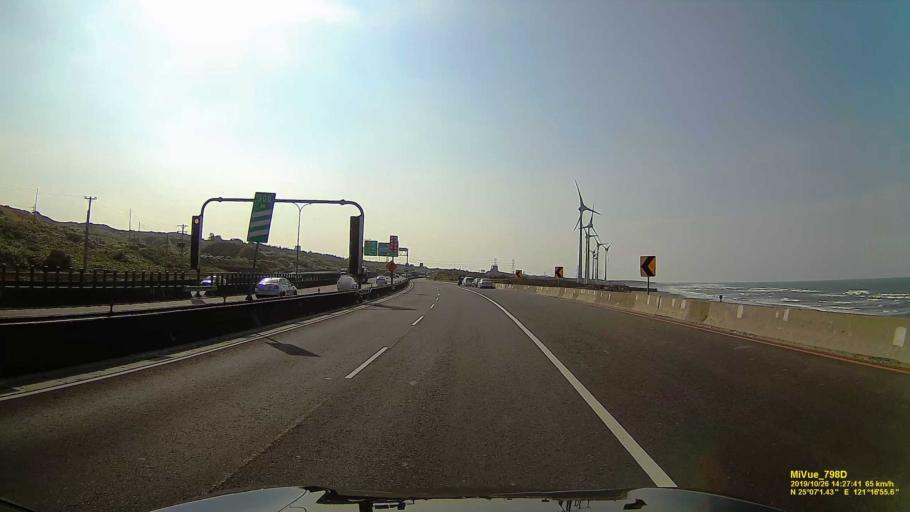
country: TW
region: Taiwan
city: Taoyuan City
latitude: 25.1170
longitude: 121.2821
